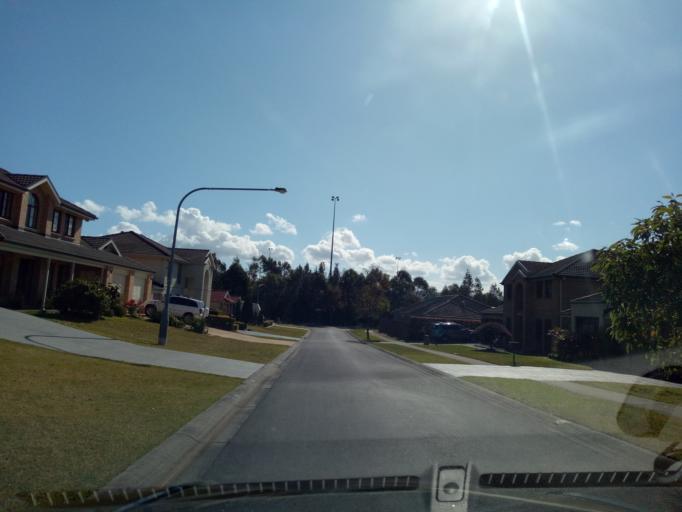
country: AU
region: New South Wales
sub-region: Gosford Shire
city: Forresters Beach
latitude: -33.3954
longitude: 151.4711
